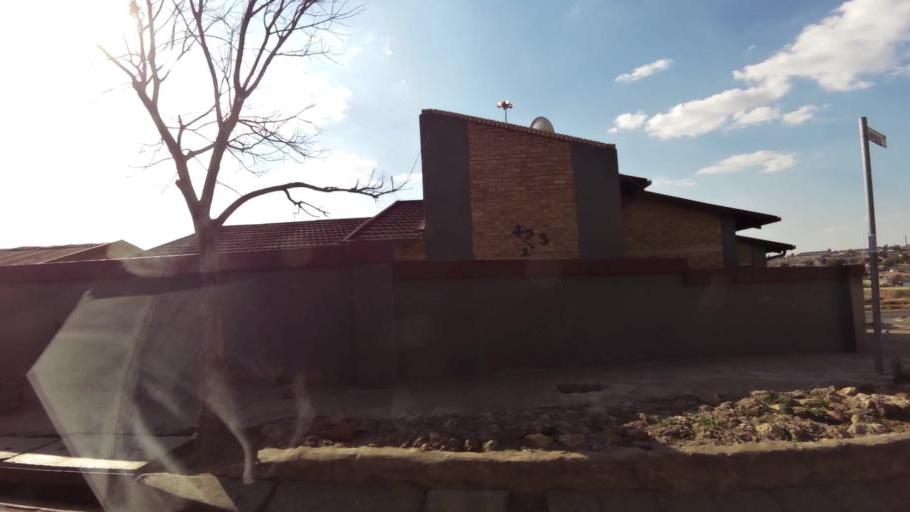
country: ZA
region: Gauteng
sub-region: City of Johannesburg Metropolitan Municipality
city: Soweto
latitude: -26.2252
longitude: 27.8785
